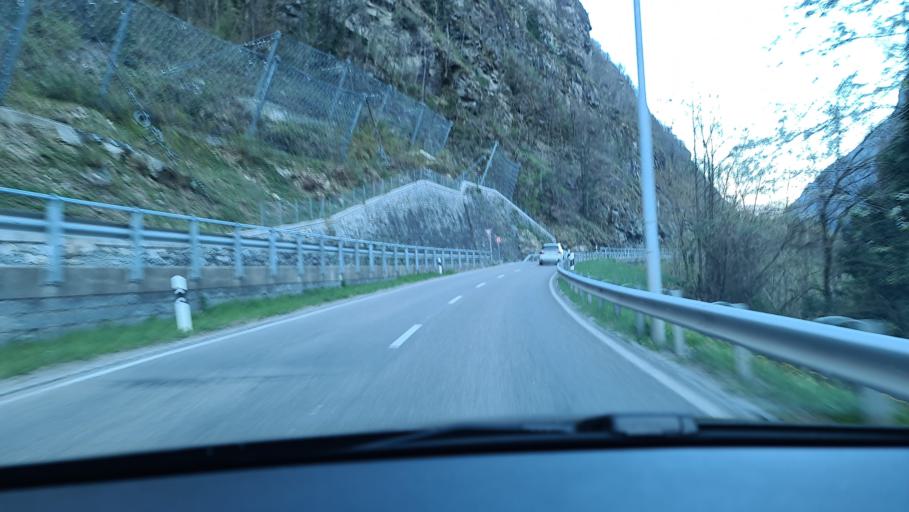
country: CH
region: Ticino
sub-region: Vallemaggia District
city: Cevio
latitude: 46.3063
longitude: 8.6140
